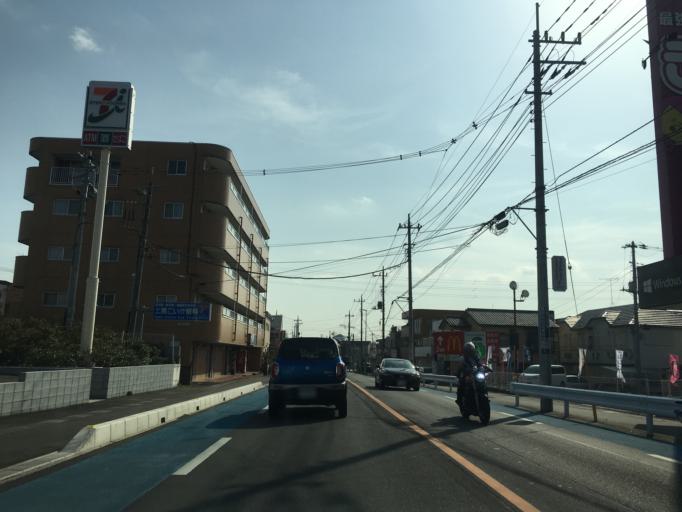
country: JP
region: Saitama
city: Ageoshimo
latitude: 35.9630
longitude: 139.5893
